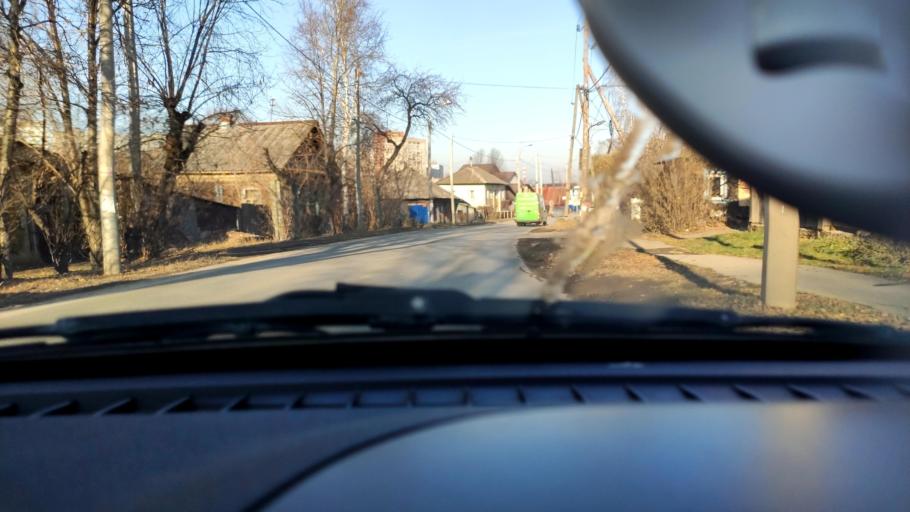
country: RU
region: Perm
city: Perm
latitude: 58.0235
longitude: 56.3126
